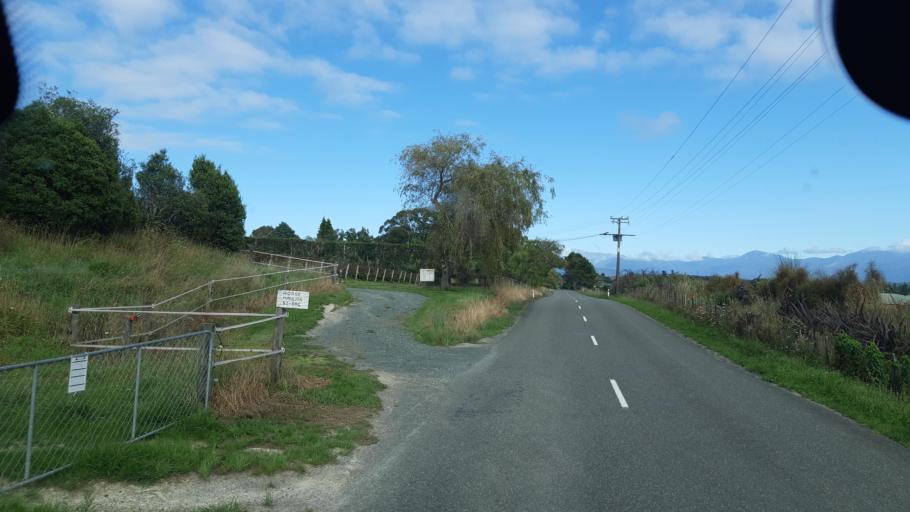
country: NZ
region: Tasman
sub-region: Tasman District
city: Mapua
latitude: -41.2411
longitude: 173.0298
